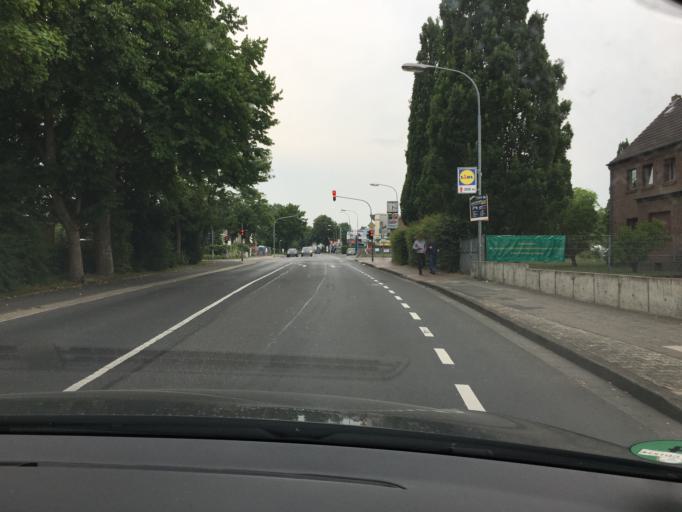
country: DE
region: North Rhine-Westphalia
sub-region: Regierungsbezirk Koln
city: Kerpen
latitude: 50.8765
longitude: 6.6932
